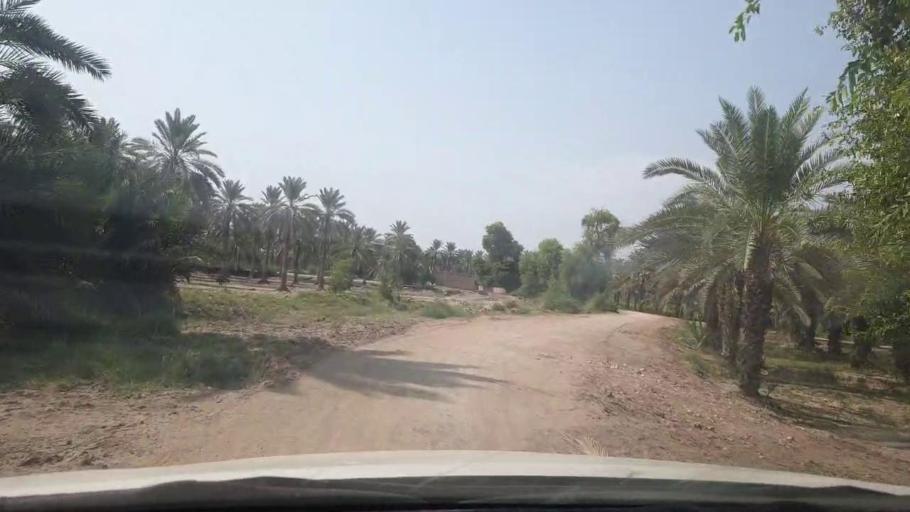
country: PK
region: Sindh
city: Rohri
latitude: 27.5930
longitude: 68.8509
